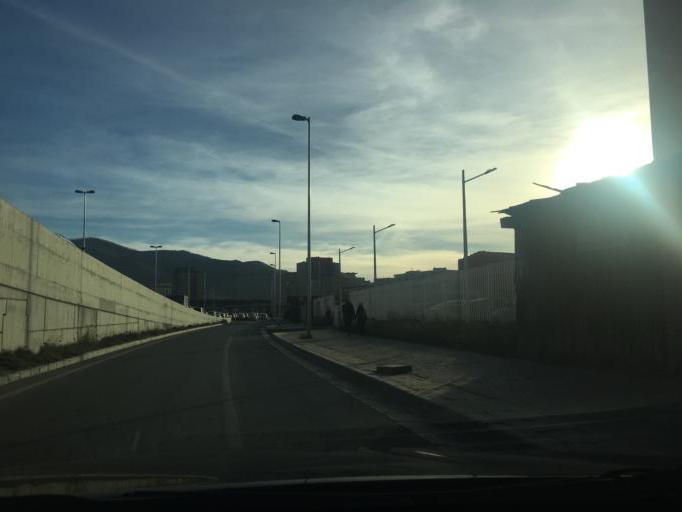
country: MN
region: Ulaanbaatar
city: Ulaanbaatar
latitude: 47.9060
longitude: 106.8942
